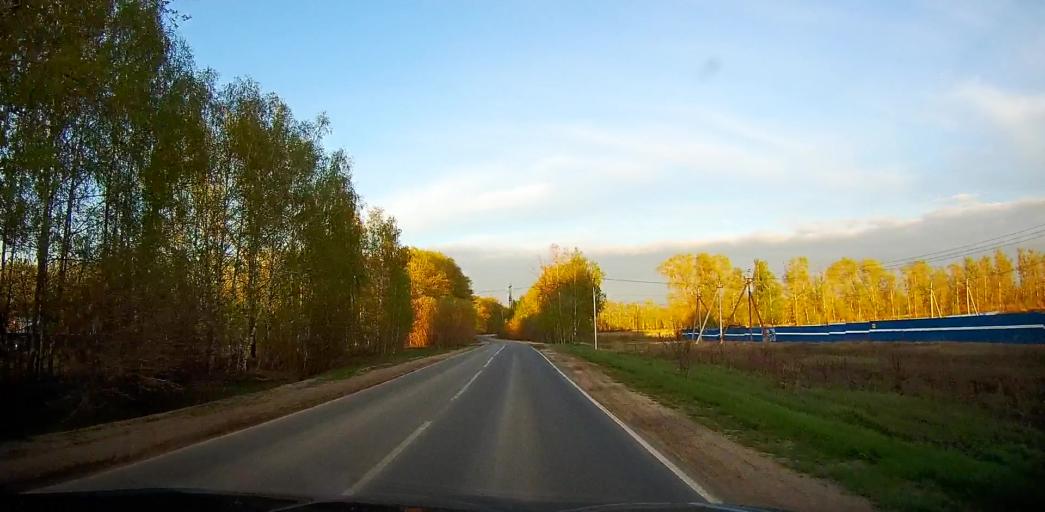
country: RU
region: Moskovskaya
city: Peski
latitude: 55.2096
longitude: 38.7077
